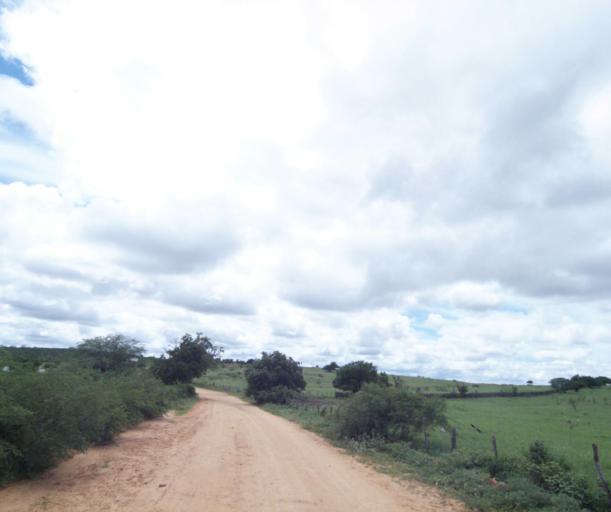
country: BR
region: Bahia
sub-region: Tanhacu
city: Tanhacu
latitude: -14.1560
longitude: -41.1925
